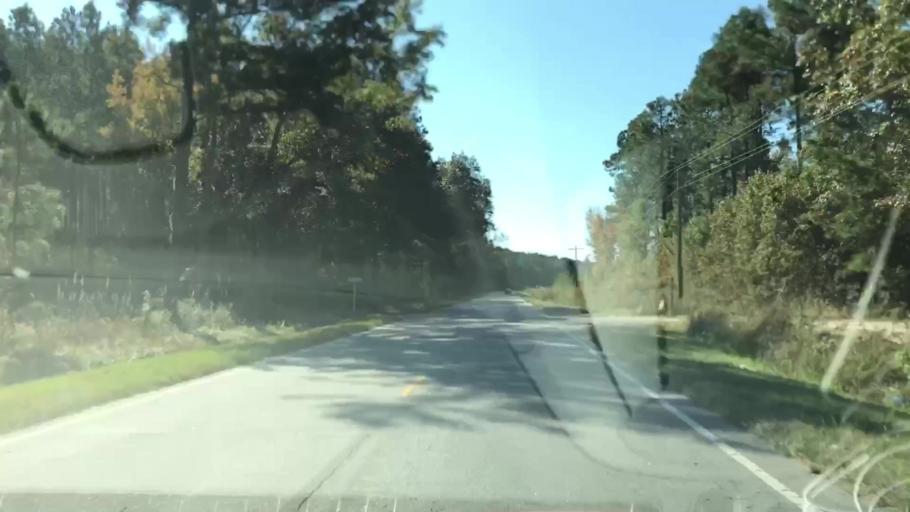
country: US
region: South Carolina
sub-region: Jasper County
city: Ridgeland
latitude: 32.4173
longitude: -80.8994
